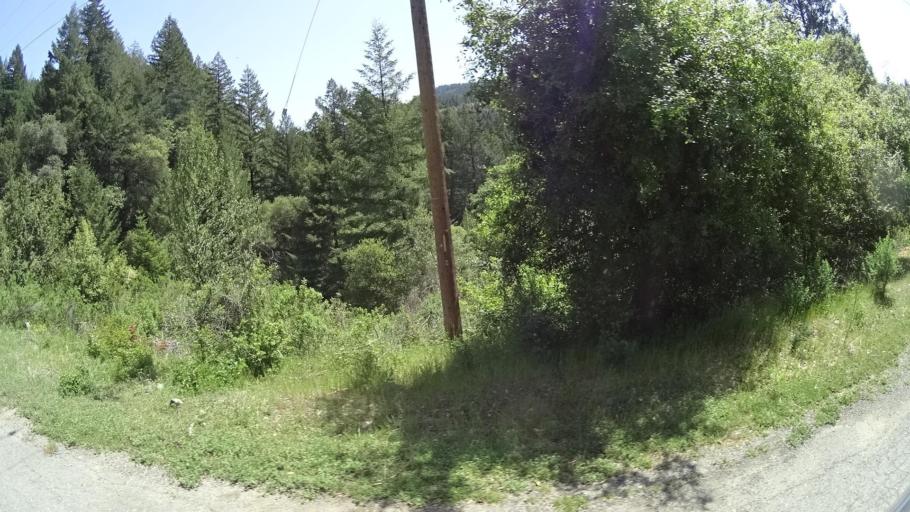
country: US
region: California
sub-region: Humboldt County
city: Redway
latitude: 40.1943
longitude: -123.5607
